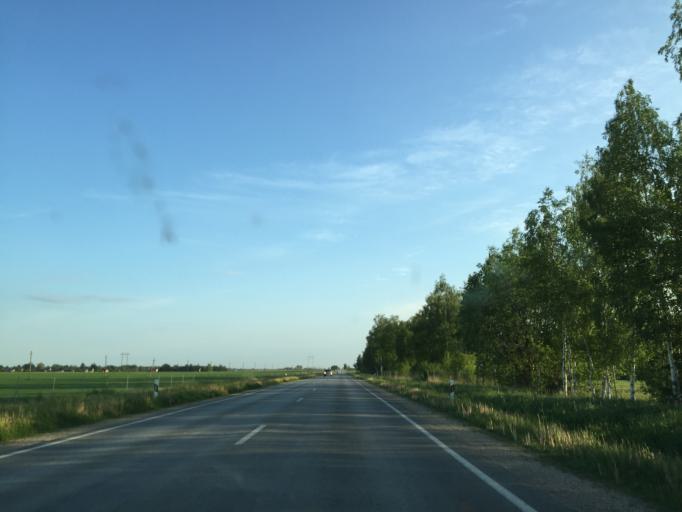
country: LT
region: Siauliu apskritis
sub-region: Joniskis
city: Joniskis
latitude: 56.1182
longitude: 23.4965
